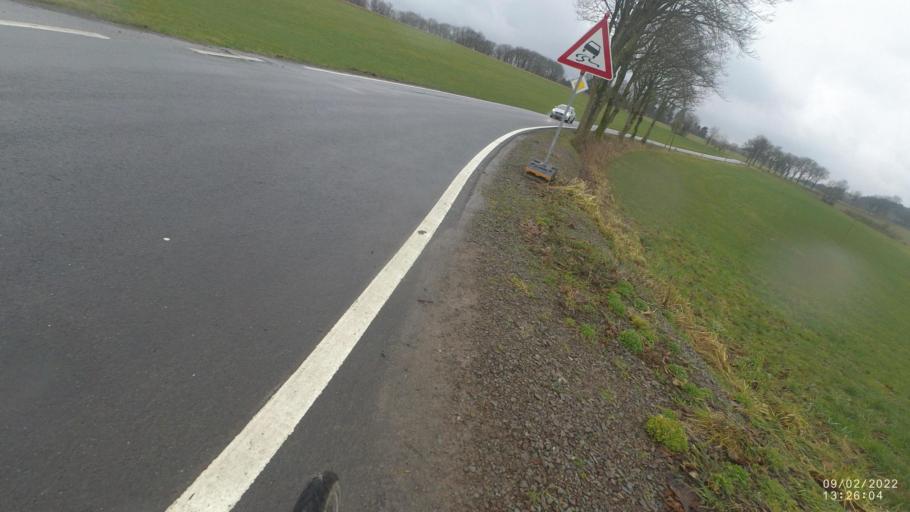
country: DE
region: North Rhine-Westphalia
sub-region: Regierungsbezirk Arnsberg
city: Schalksmuhle
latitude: 51.2194
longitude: 7.5070
